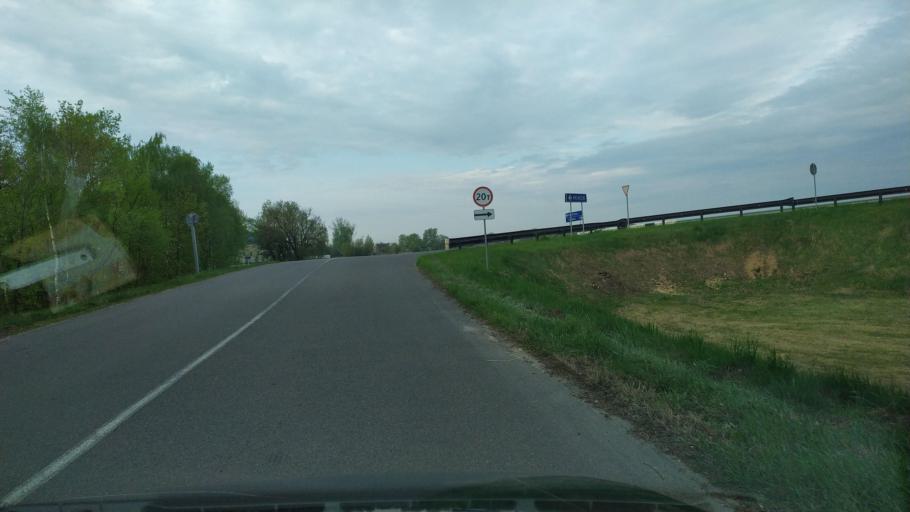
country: BY
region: Brest
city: Zhabinka
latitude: 52.1604
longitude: 24.0867
